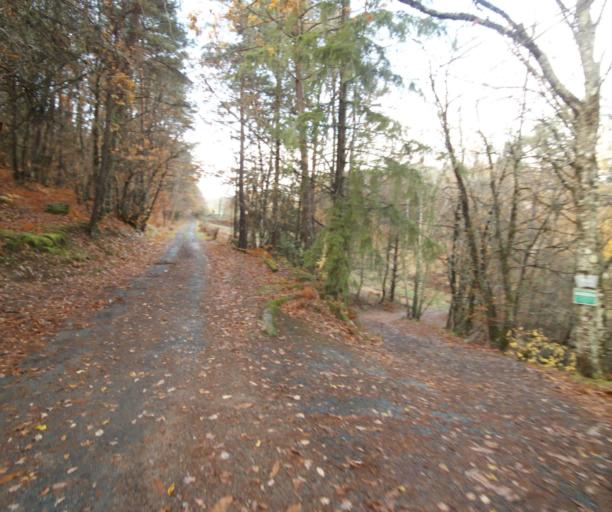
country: FR
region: Limousin
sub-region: Departement de la Correze
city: Cornil
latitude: 45.2154
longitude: 1.6790
